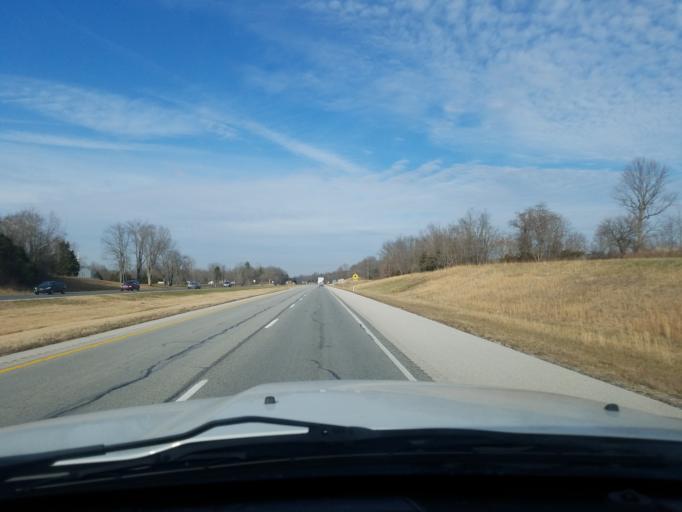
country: US
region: Indiana
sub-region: Monroe County
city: Bloomington
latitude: 39.0666
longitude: -86.5361
